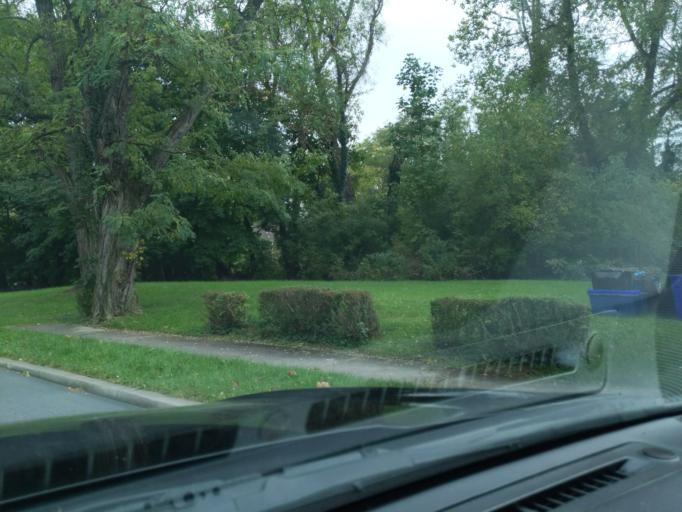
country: US
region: Pennsylvania
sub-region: Blair County
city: Lakemont
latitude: 40.4930
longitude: -78.4071
